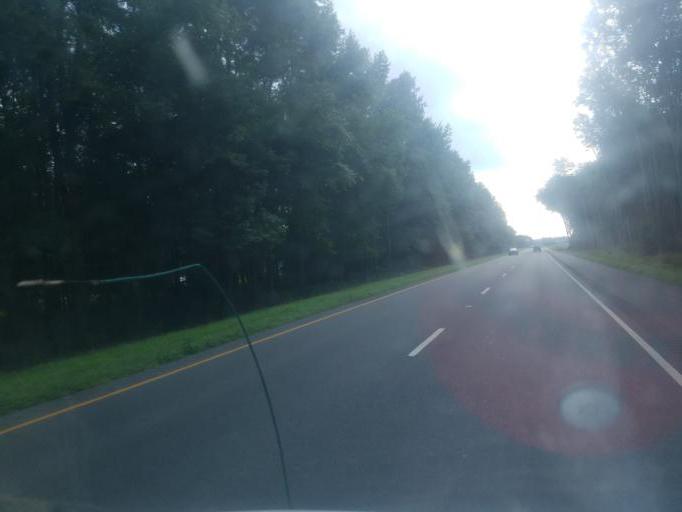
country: US
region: Maryland
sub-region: Wicomico County
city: Pittsville
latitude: 38.3850
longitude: -75.3999
